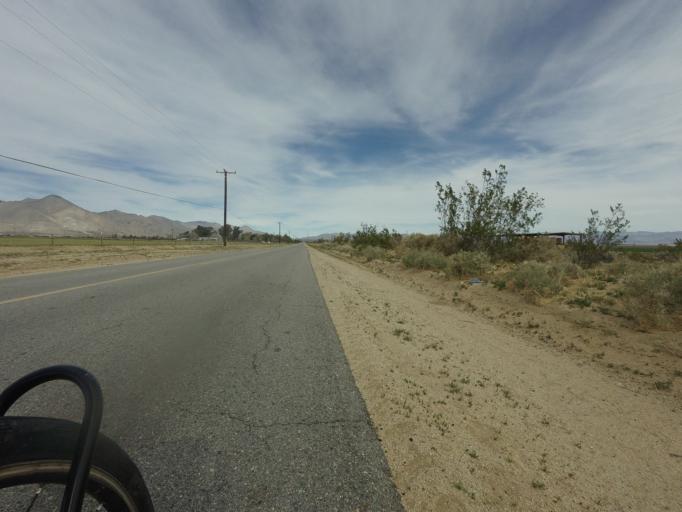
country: US
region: California
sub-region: Kern County
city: Inyokern
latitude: 35.7449
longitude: -117.8414
